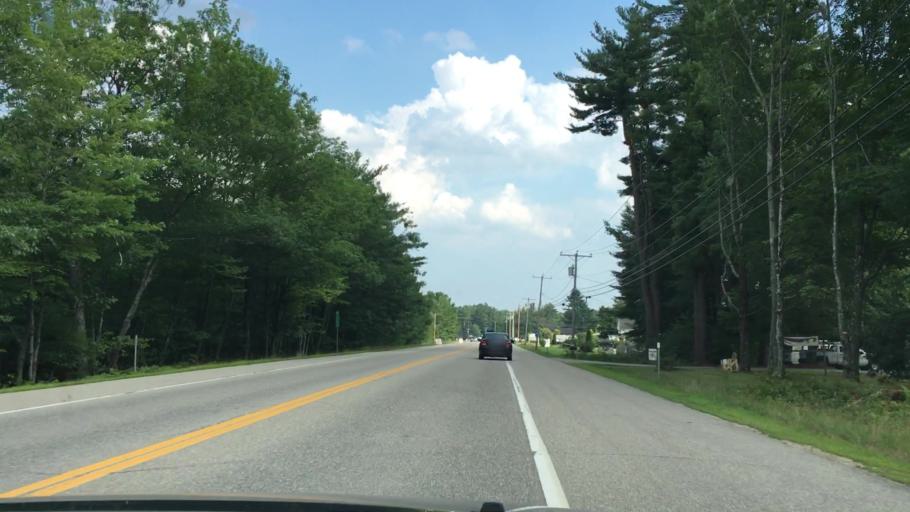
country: US
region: New Hampshire
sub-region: Strafford County
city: Farmington
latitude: 43.3457
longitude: -71.0226
